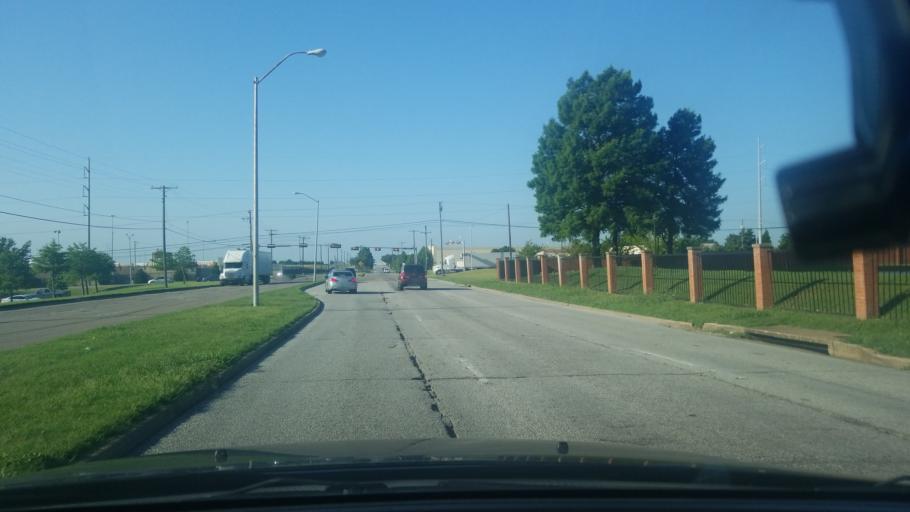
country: US
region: Texas
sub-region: Dallas County
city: Mesquite
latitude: 32.7936
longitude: -96.6684
